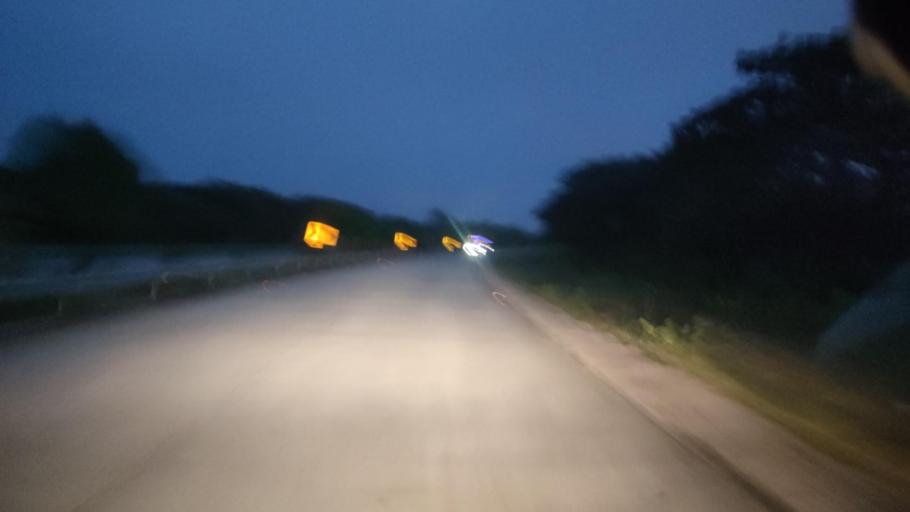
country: MM
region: Mandalay
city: Nay Pyi Taw
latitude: 19.9822
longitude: 95.9846
